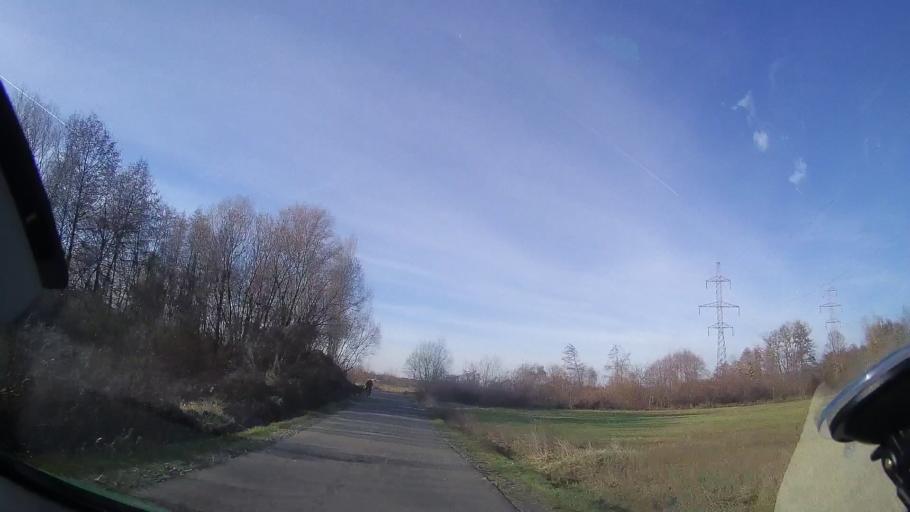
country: RO
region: Bihor
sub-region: Comuna Auseu
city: Grosi
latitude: 47.0272
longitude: 22.4788
